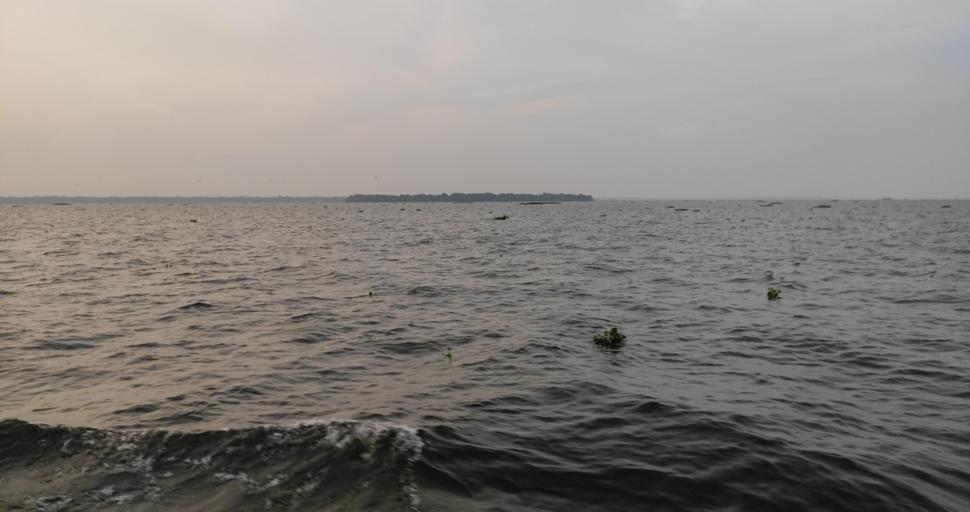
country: IN
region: Kerala
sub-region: Alappuzha
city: Shertallai
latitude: 9.6028
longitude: 76.3930
